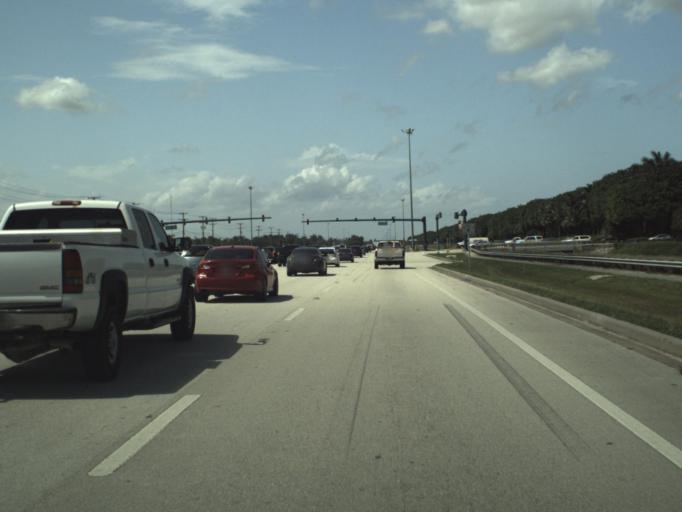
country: US
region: Florida
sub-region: Palm Beach County
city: Wellington
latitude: 26.6343
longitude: -80.2040
